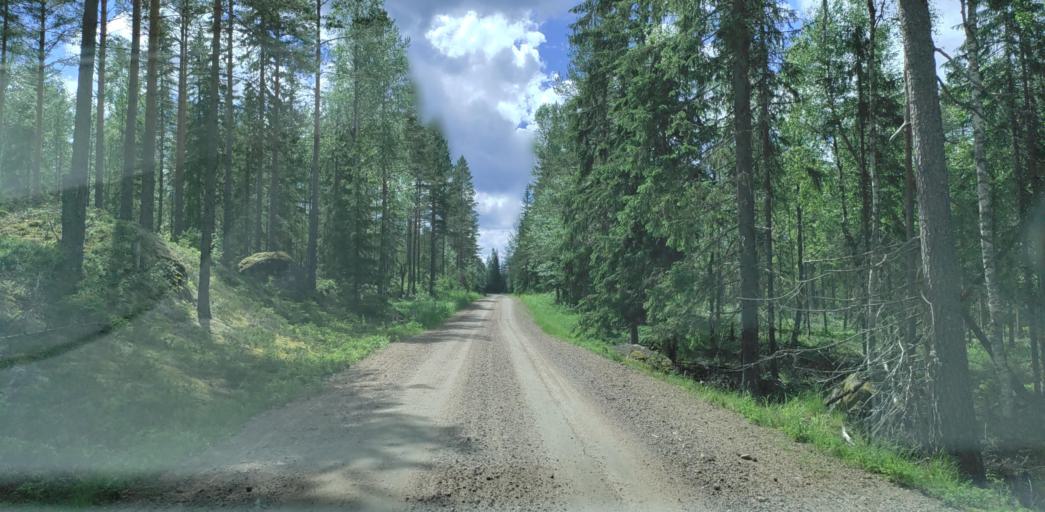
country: SE
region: Vaermland
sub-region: Hagfors Kommun
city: Ekshaerad
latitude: 60.0986
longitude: 13.3492
